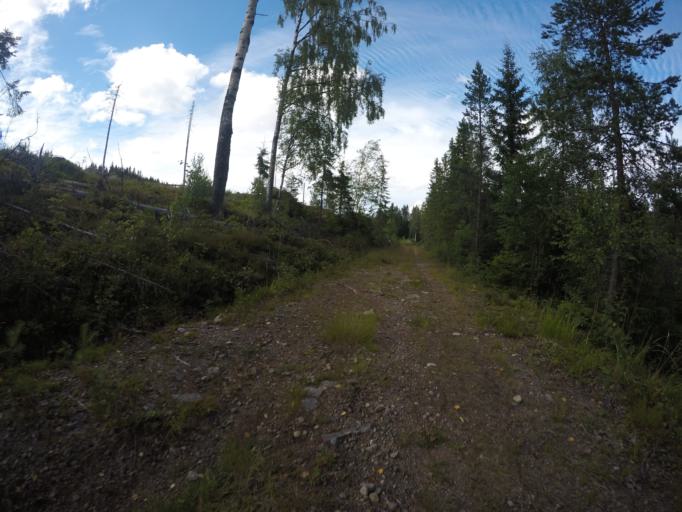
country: SE
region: Dalarna
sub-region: Ludvika Kommun
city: Abborrberget
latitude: 60.0171
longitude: 14.5984
